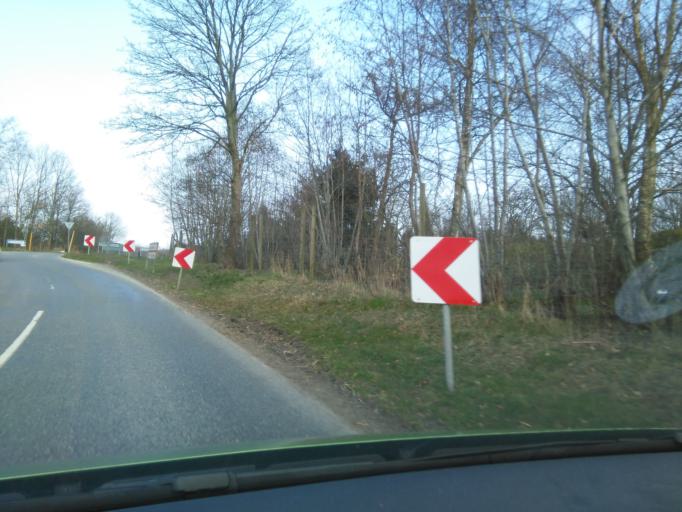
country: DK
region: Central Jutland
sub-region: Arhus Kommune
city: Beder
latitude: 56.0594
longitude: 10.2427
